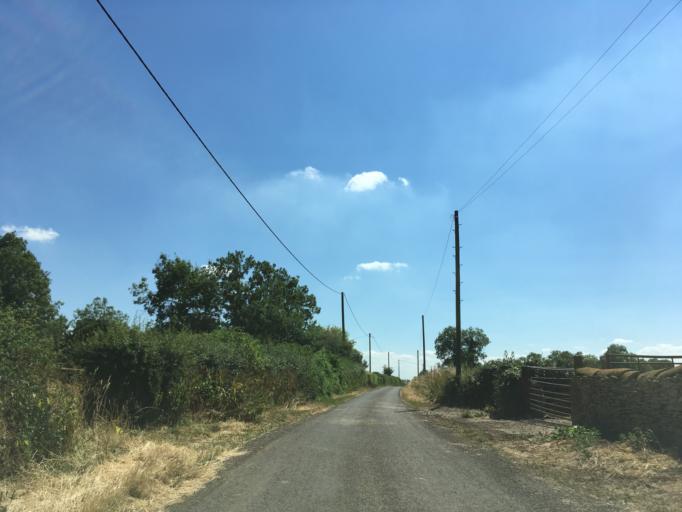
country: GB
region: England
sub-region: Wiltshire
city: Luckington
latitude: 51.5645
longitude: -2.2133
